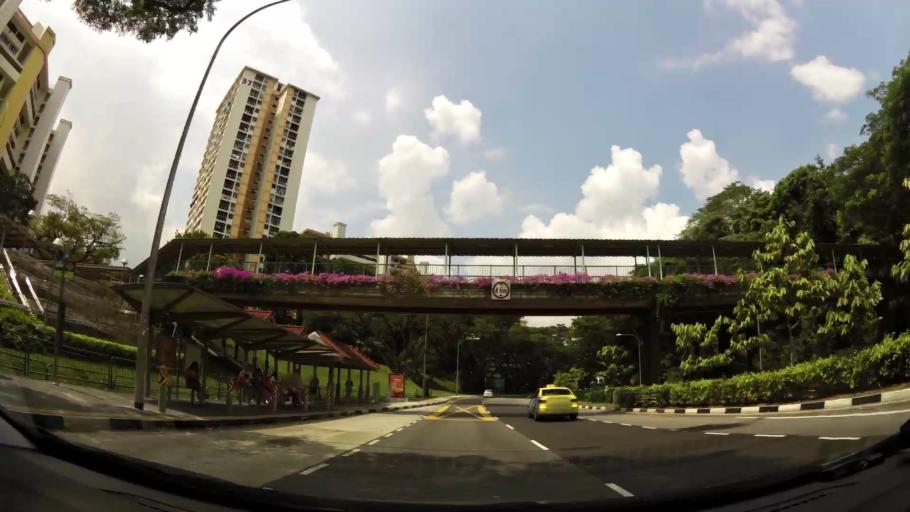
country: SG
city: Singapore
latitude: 1.2725
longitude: 103.8238
